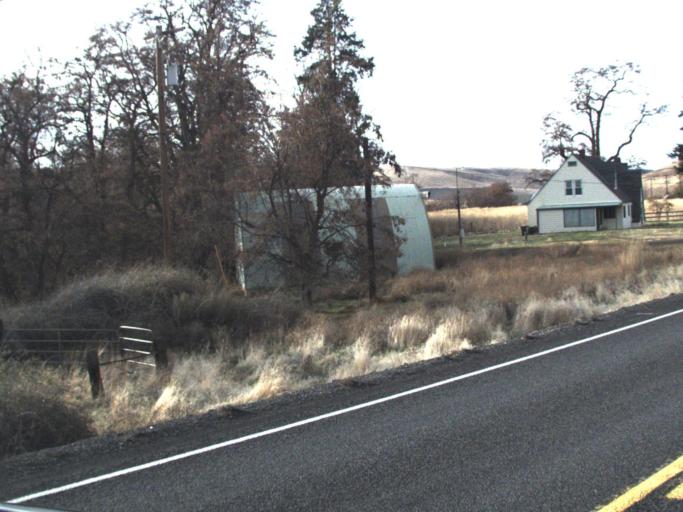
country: US
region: Washington
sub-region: Garfield County
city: Pomeroy
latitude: 46.5199
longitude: -117.7993
